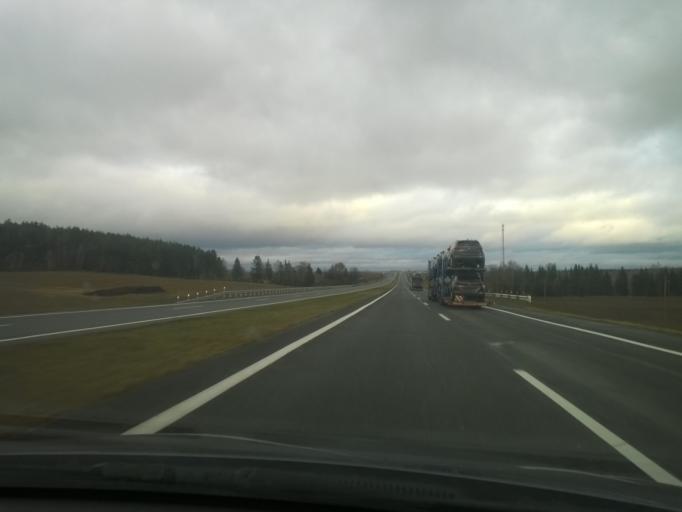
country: BY
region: Minsk
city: Snow
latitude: 53.2930
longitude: 26.3510
